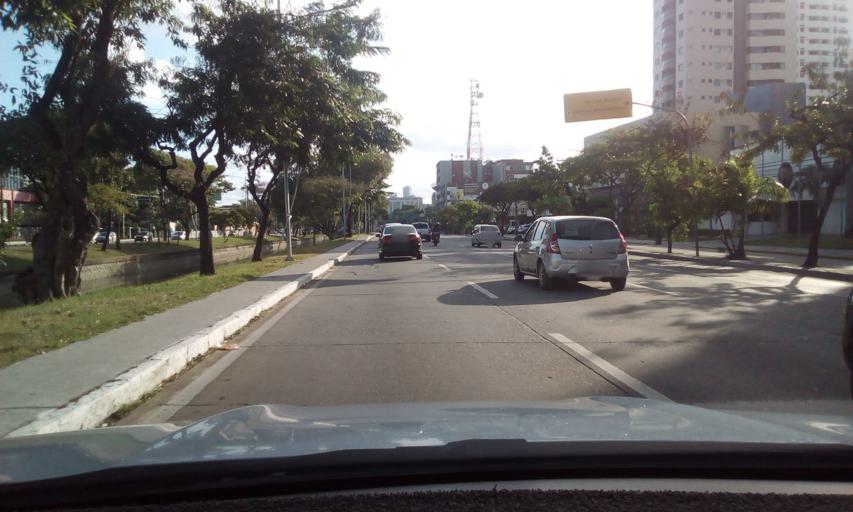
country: BR
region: Pernambuco
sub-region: Recife
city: Recife
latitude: -8.0488
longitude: -34.8932
